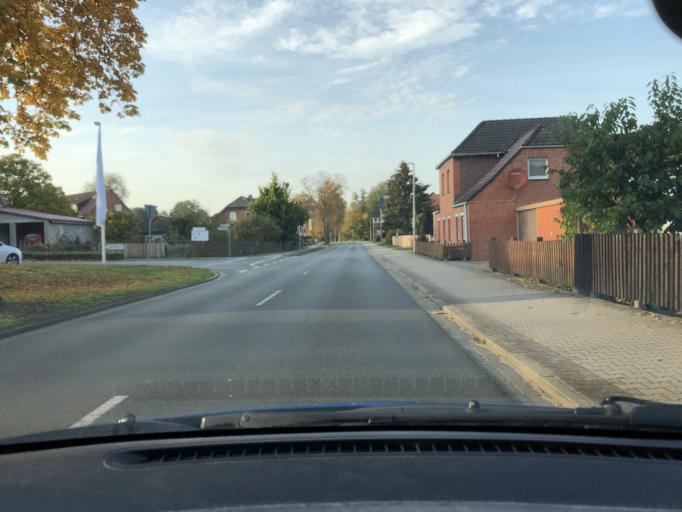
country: DE
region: Lower Saxony
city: Hitzacker
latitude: 53.1407
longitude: 11.0440
